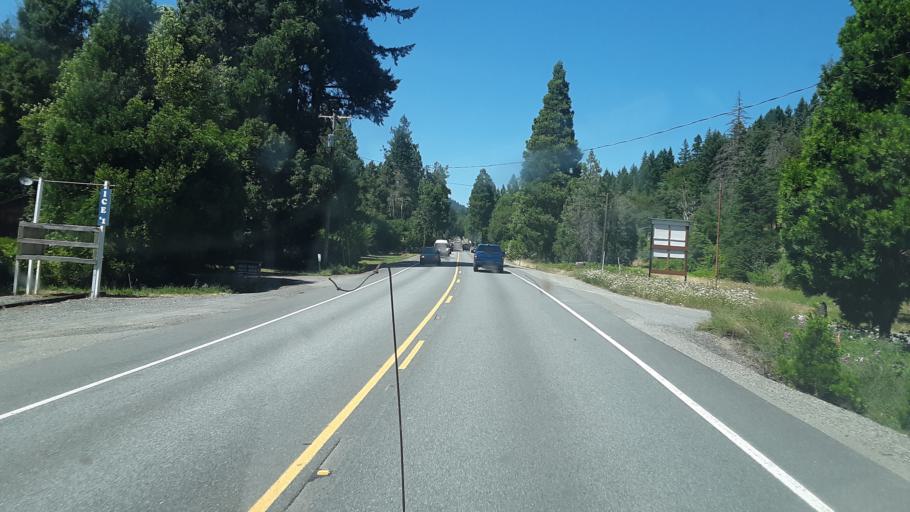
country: US
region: Oregon
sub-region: Josephine County
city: Cave Junction
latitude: 42.2894
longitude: -123.6124
